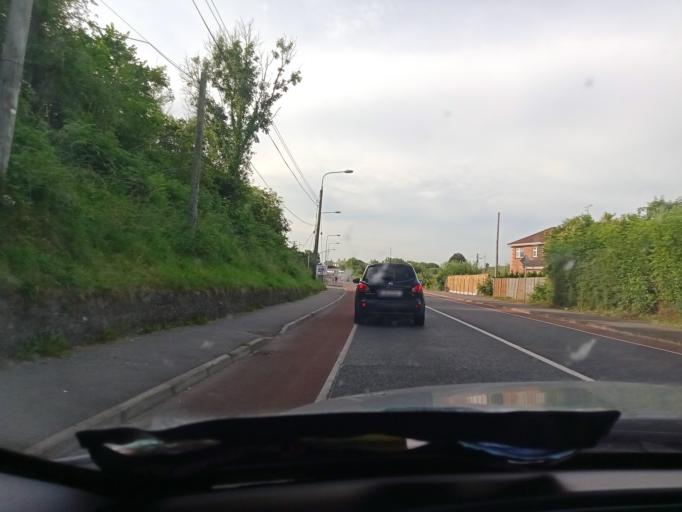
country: IE
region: Ulster
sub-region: An Cabhan
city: Cavan
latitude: 53.9772
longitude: -7.3545
